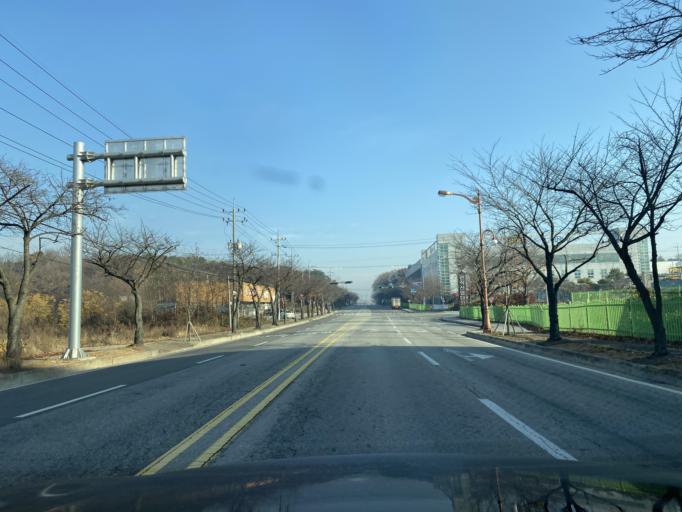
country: KR
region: Chungcheongnam-do
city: Yesan
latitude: 36.7138
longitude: 126.8418
